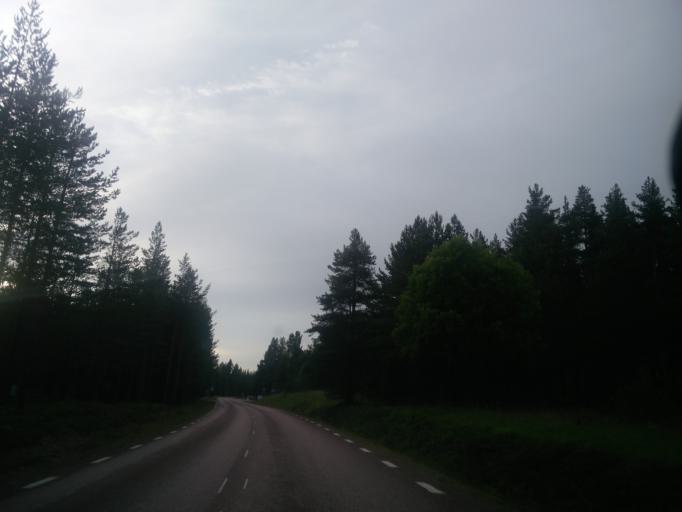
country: NO
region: Hedmark
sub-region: Trysil
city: Innbygda
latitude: 61.7940
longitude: 12.9231
